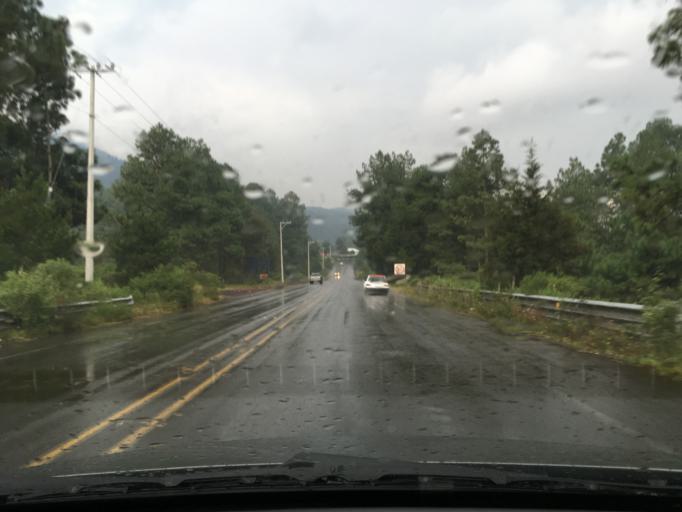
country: MX
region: Michoacan
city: Angahuan
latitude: 19.5484
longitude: -102.2145
